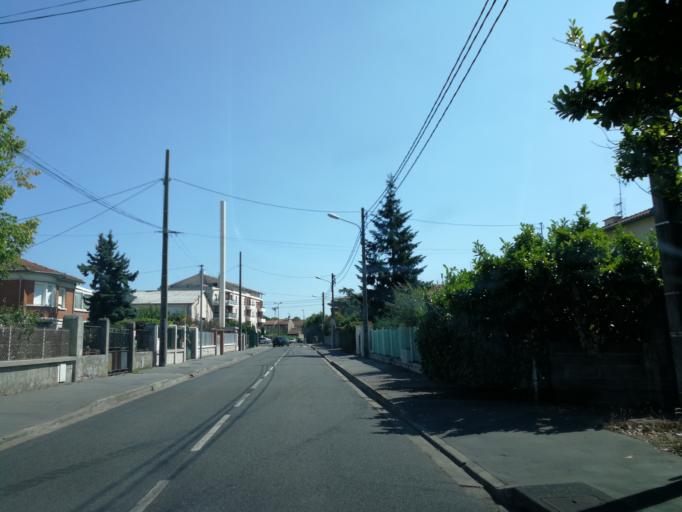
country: FR
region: Midi-Pyrenees
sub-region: Departement de la Haute-Garonne
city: Toulouse
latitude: 43.6341
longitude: 1.4568
